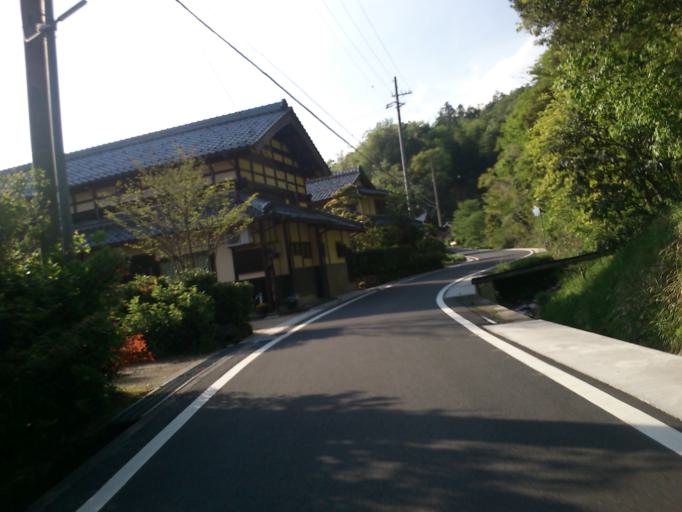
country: JP
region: Kyoto
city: Miyazu
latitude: 35.6125
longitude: 135.1337
